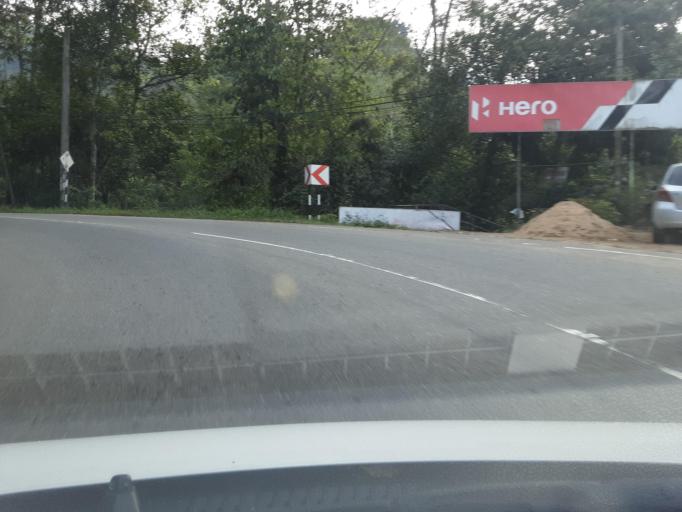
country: LK
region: Uva
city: Badulla
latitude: 6.9539
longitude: 81.0239
